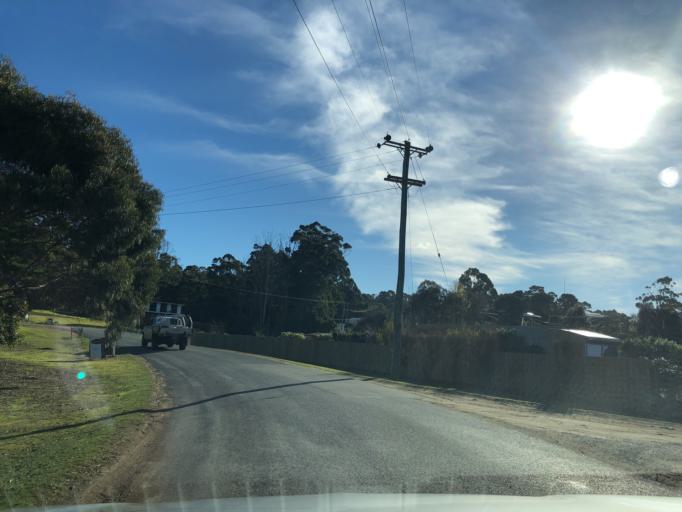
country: AU
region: Tasmania
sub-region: Kingborough
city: Kettering
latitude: -43.3577
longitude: 147.3261
